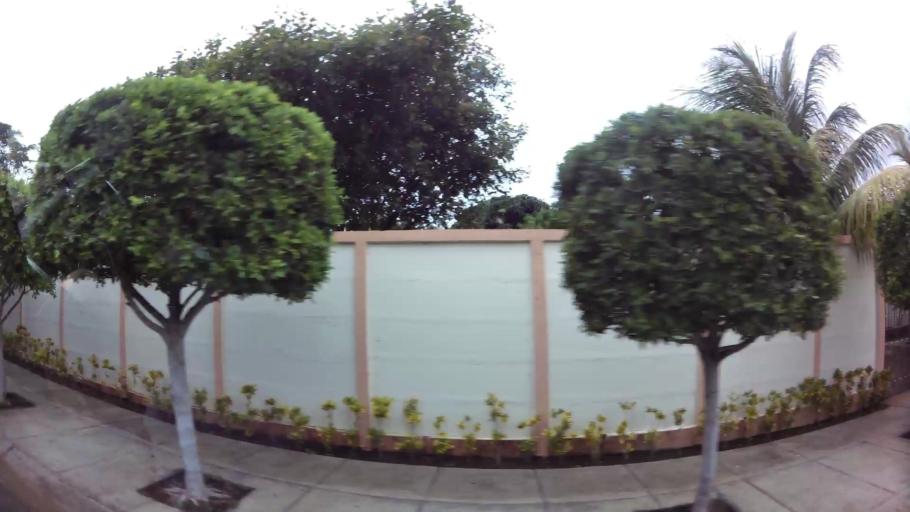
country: NI
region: Masaya
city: Ticuantepe
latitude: 12.0531
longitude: -86.1923
